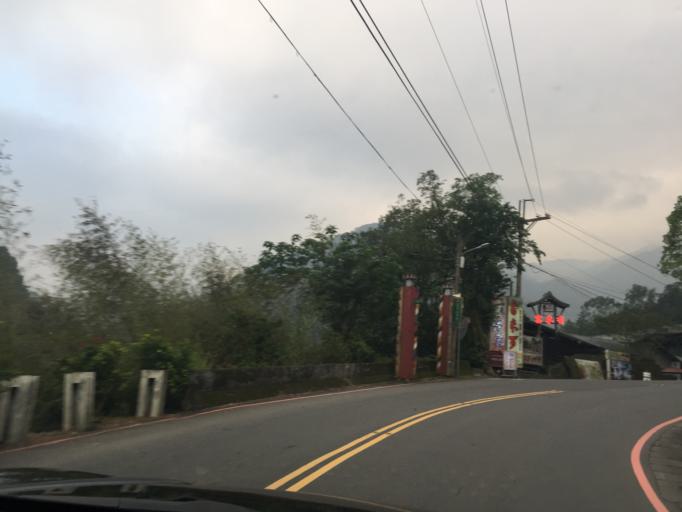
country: TW
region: Taipei
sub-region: Taipei
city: Banqiao
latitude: 24.8629
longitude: 121.5494
